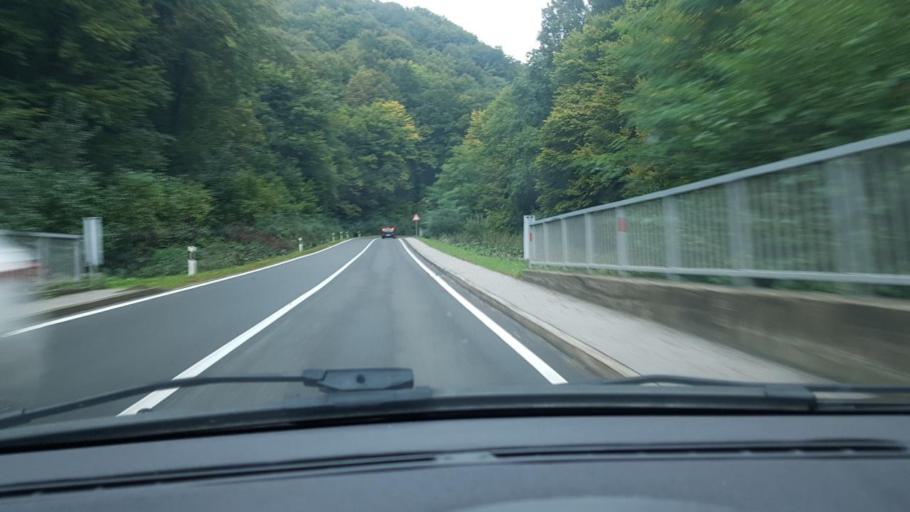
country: HR
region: Krapinsko-Zagorska
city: Marija Bistrica
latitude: 45.9434
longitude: 16.1050
